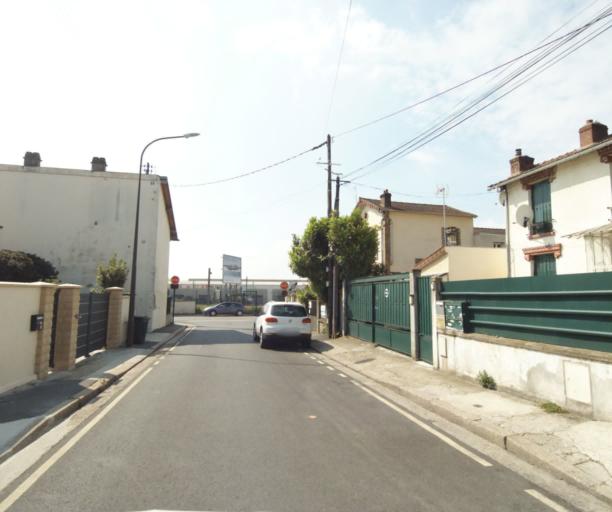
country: FR
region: Ile-de-France
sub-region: Departement du Val-d'Oise
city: Argenteuil
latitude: 48.9563
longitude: 2.2454
